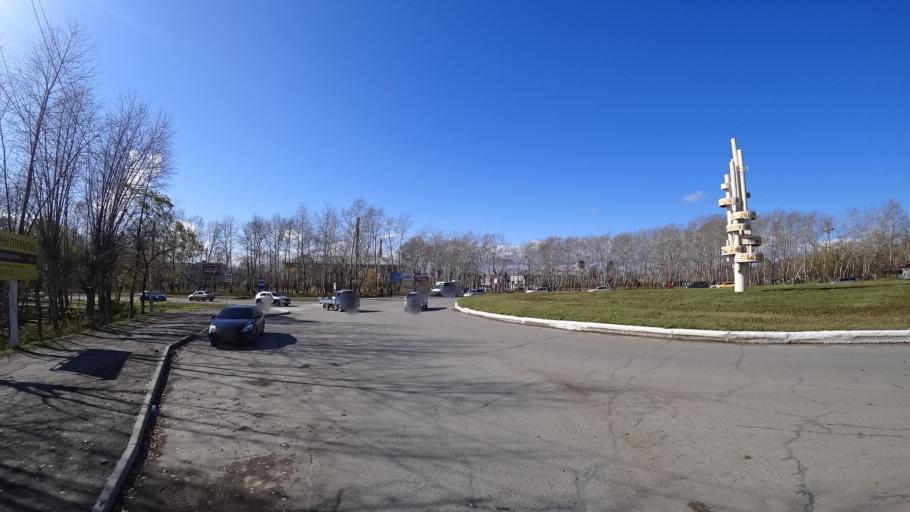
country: RU
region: Khabarovsk Krai
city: Amursk
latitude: 50.2296
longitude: 136.9020
